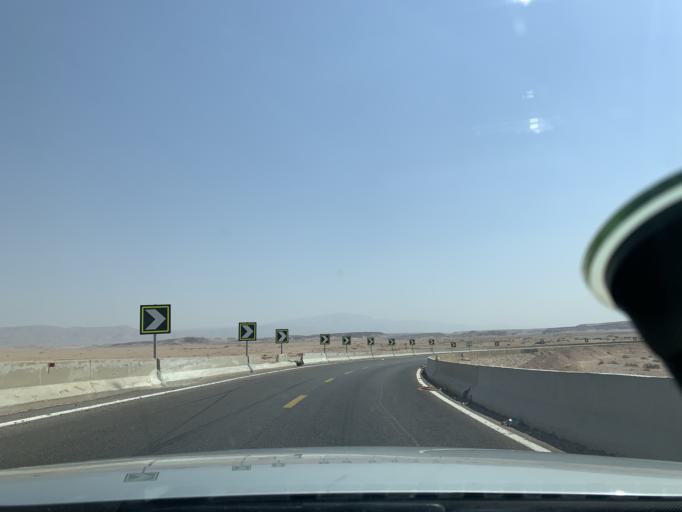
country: EG
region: As Suways
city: Ain Sukhna
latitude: 29.1064
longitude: 32.5336
